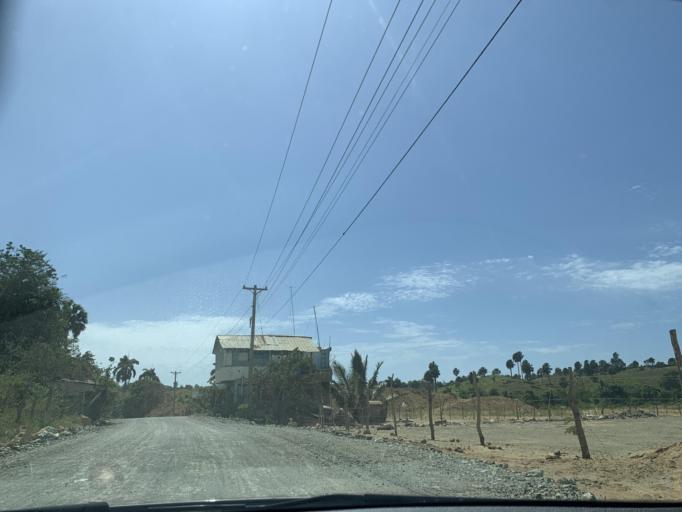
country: DO
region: Puerto Plata
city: Luperon
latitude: 19.8827
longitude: -70.8456
